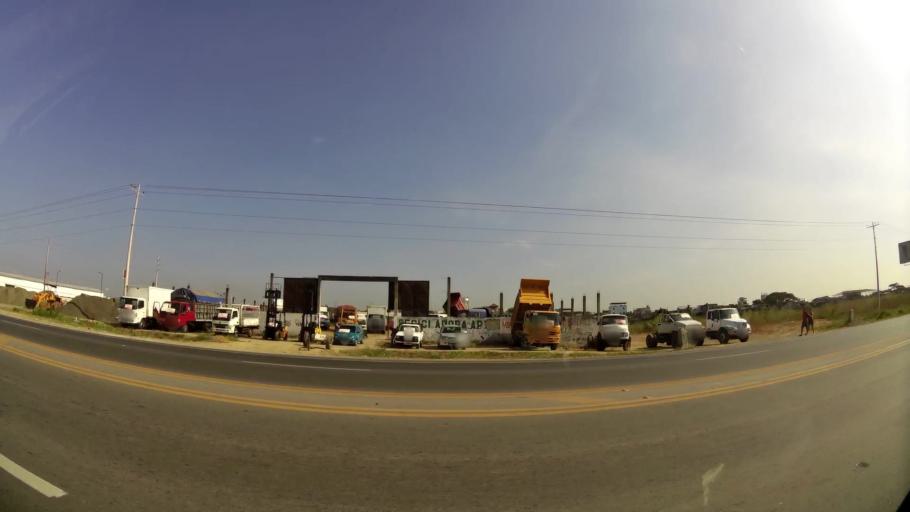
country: EC
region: Guayas
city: Eloy Alfaro
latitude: -2.1771
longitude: -79.8021
